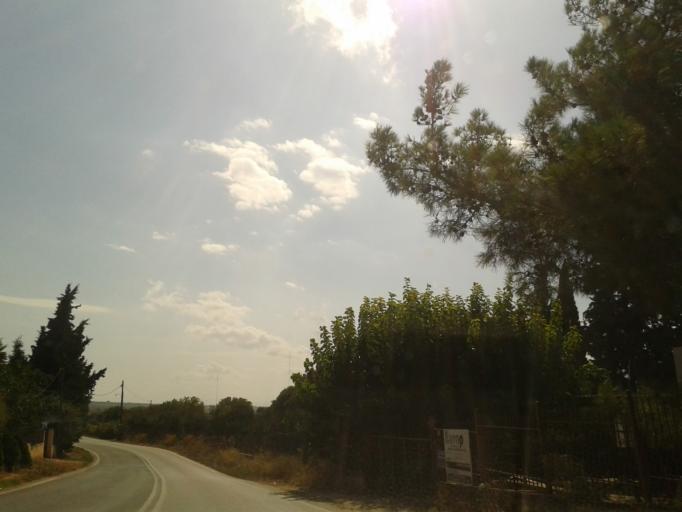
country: GR
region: Attica
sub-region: Nomarchia Anatolikis Attikis
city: Kato Soulion
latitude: 38.1737
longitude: 24.0223
